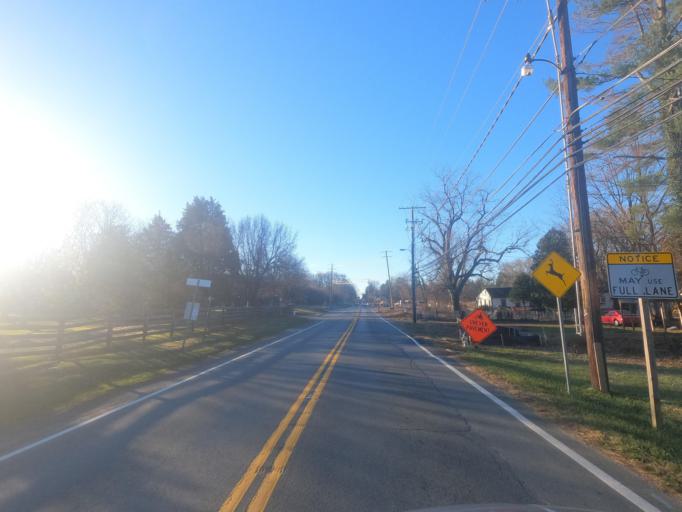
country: US
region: Maryland
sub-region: Montgomery County
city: Olney
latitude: 39.1769
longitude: -77.0584
